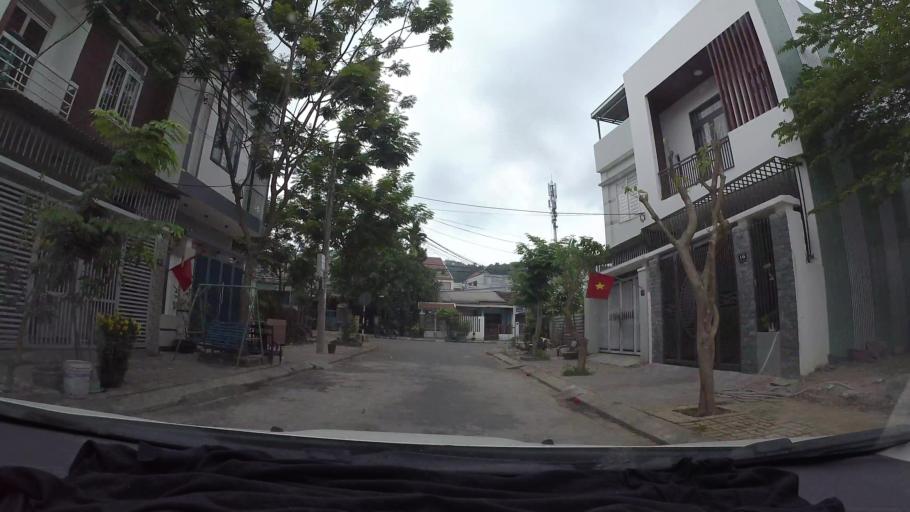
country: VN
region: Da Nang
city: Cam Le
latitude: 16.0355
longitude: 108.1748
